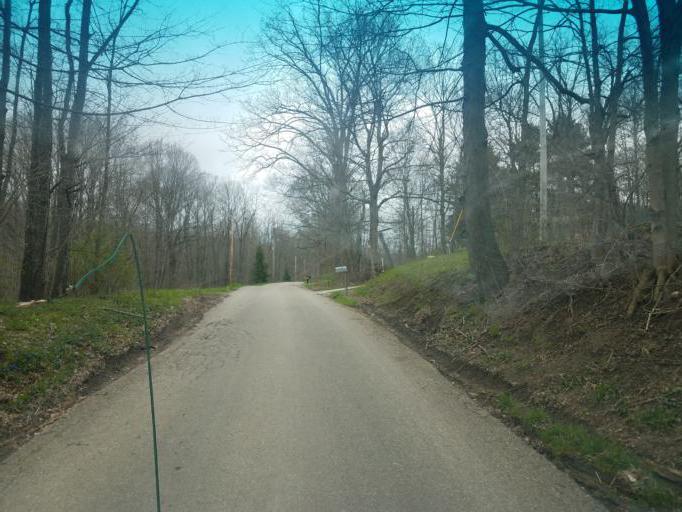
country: US
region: Ohio
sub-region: Stark County
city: Beach City
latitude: 40.6136
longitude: -81.6581
